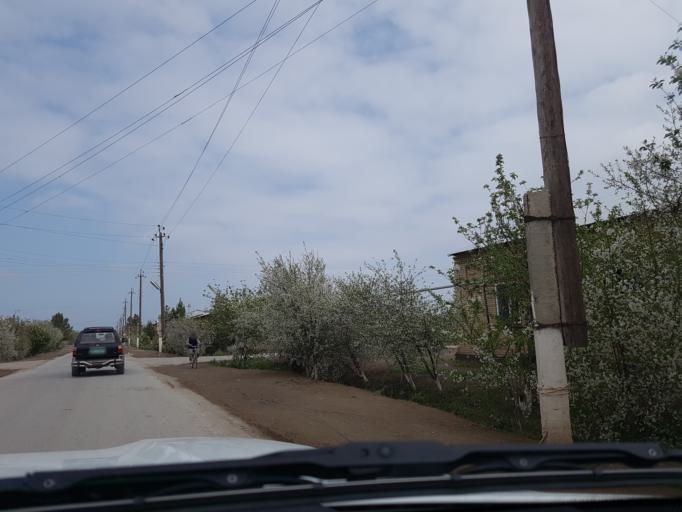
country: TM
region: Lebap
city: Turkmenabat
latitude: 38.9721
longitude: 63.6868
